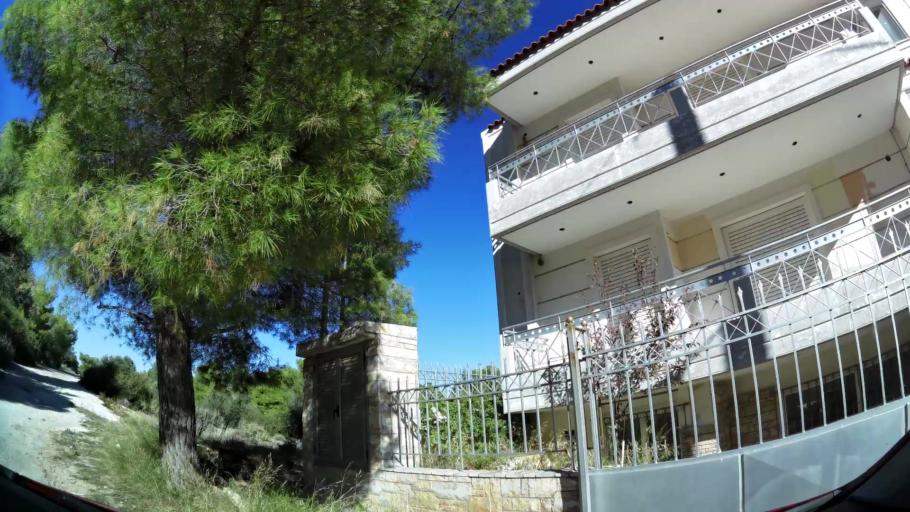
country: GR
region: Attica
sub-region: Nomarchia Anatolikis Attikis
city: Leondarion
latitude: 37.9891
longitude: 23.8423
